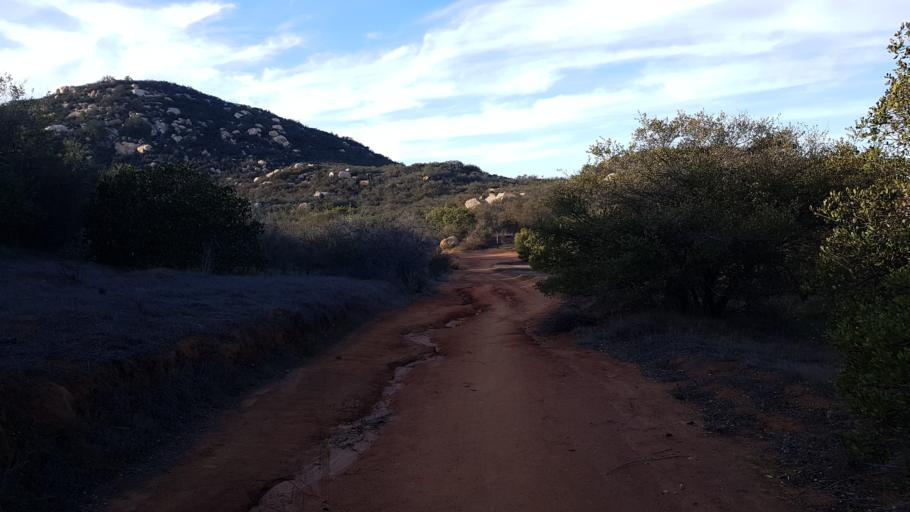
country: US
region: California
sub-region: San Diego County
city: Valley Center
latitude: 33.2010
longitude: -117.0617
